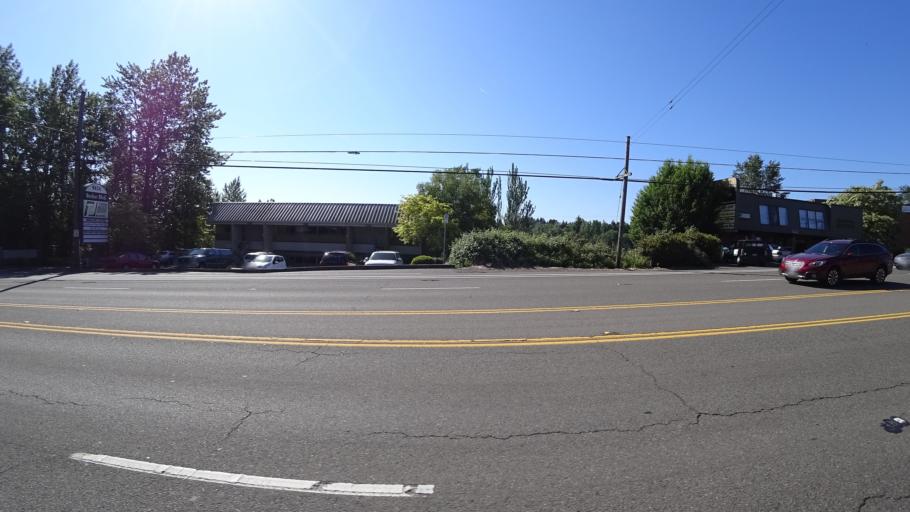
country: US
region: Oregon
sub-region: Washington County
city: Garden Home-Whitford
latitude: 45.4573
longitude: -122.7124
